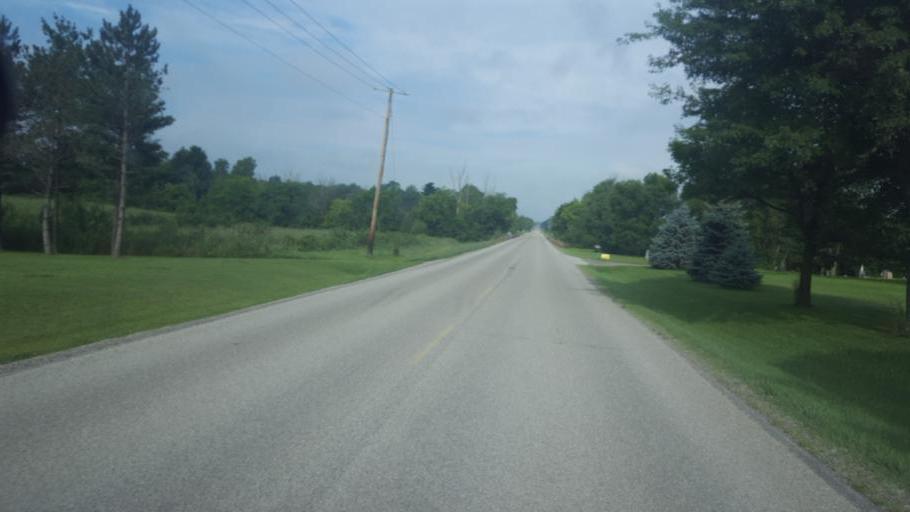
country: US
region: Ohio
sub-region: Delaware County
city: Ashley
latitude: 40.4070
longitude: -82.9008
